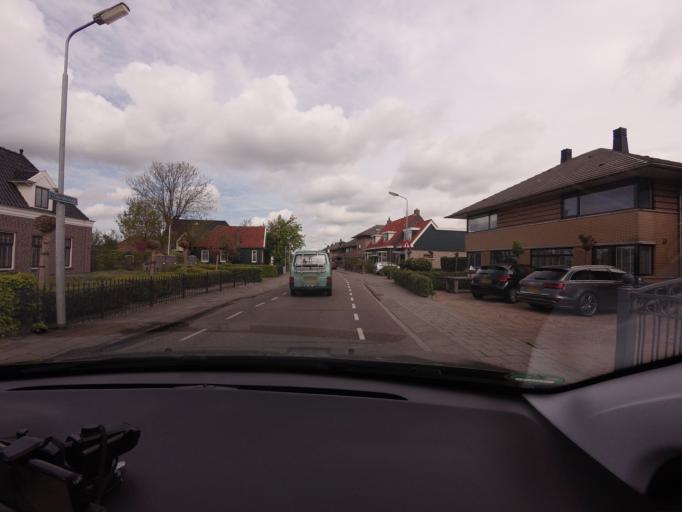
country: NL
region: North Holland
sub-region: Gemeente Landsmeer
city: Landsmeer
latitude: 52.4454
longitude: 4.8729
